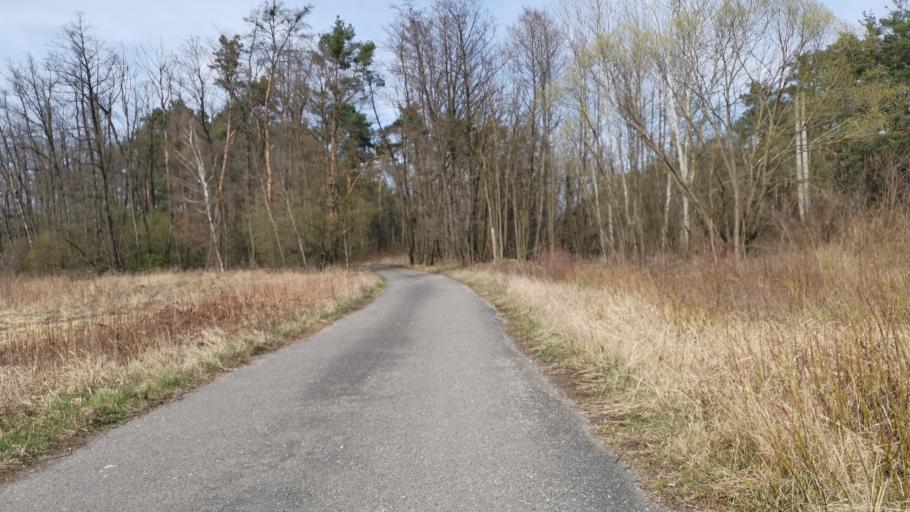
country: SK
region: Trnavsky
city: Gbely
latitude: 48.6728
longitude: 17.0549
